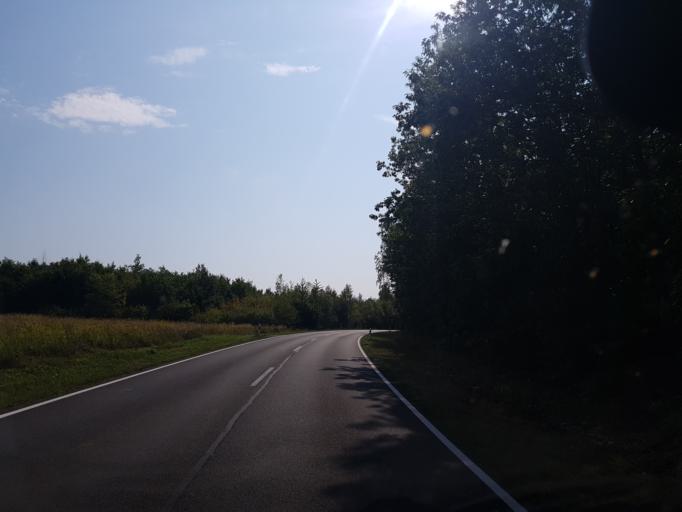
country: DE
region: Brandenburg
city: Lauchhammer
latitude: 51.5296
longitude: 13.7127
